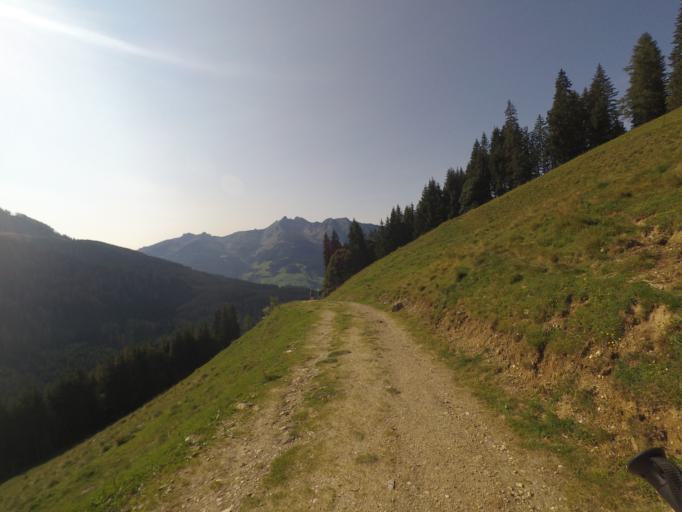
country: AT
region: Salzburg
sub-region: Politischer Bezirk Sankt Johann im Pongau
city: Kleinarl
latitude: 47.2719
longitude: 13.2572
